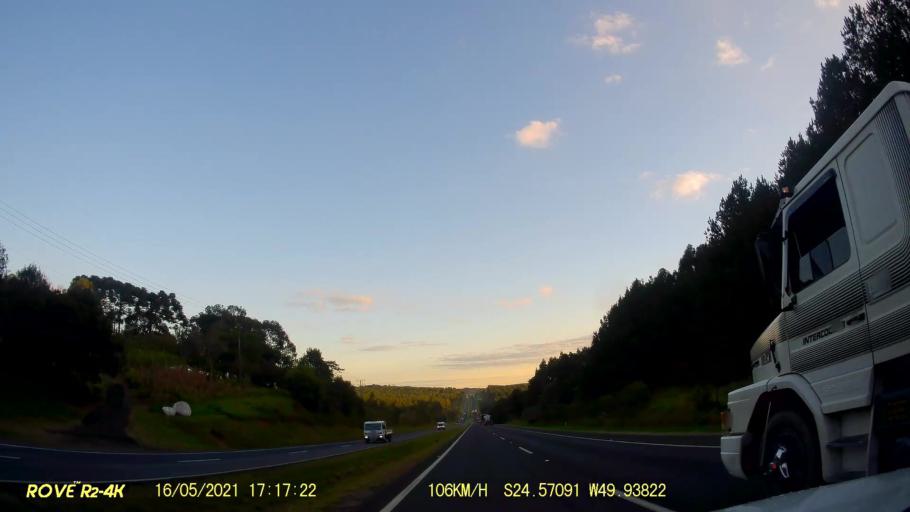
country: BR
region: Parana
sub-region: Pirai Do Sul
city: Pirai do Sul
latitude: -24.5711
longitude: -49.9384
